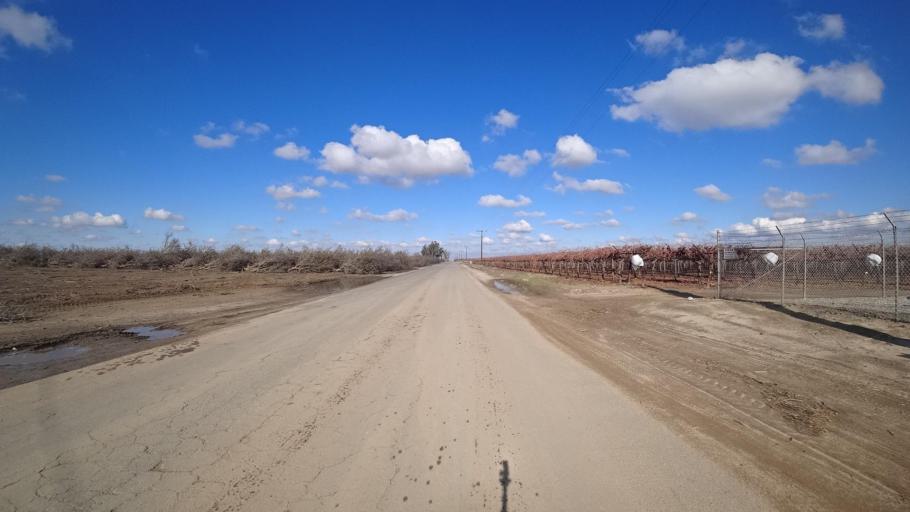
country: US
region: California
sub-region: Kern County
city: Delano
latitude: 35.7395
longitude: -119.3657
